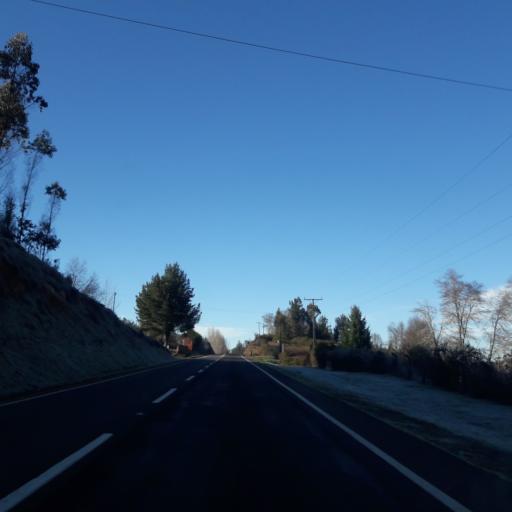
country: CL
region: Biobio
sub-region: Provincia de Biobio
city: La Laja
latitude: -37.3217
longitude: -72.9185
